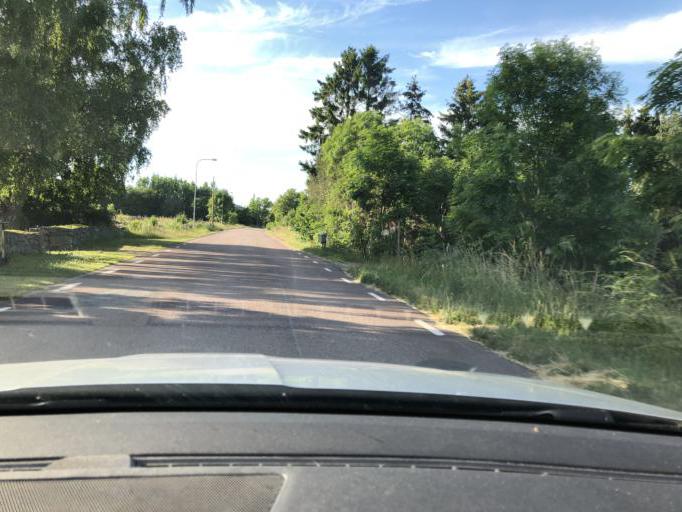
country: SE
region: Blekinge
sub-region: Solvesborgs Kommun
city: Soelvesborg
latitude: 56.1484
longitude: 14.6032
